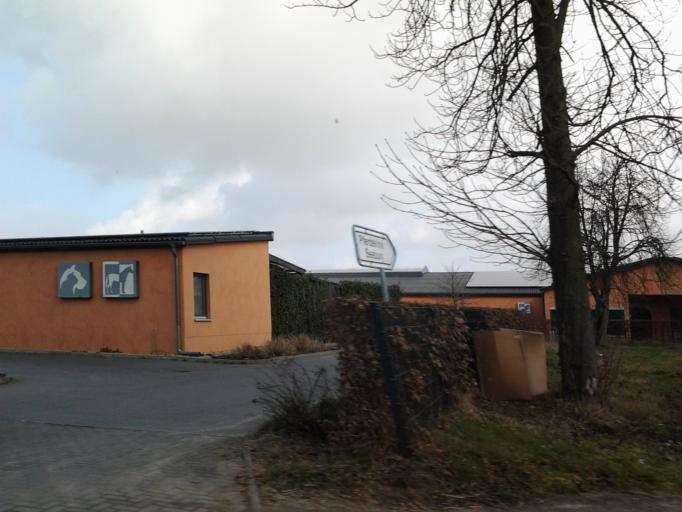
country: DE
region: Berlin
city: Staaken
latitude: 52.5075
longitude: 13.1455
